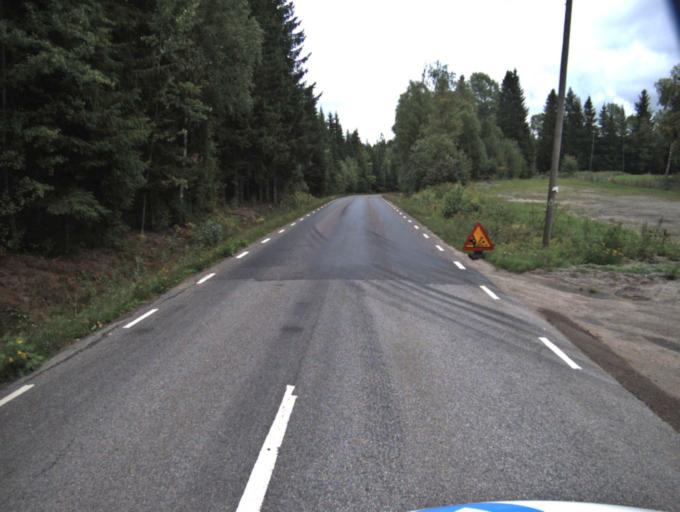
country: SE
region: Vaestra Goetaland
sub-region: Ulricehamns Kommun
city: Ulricehamn
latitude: 57.7699
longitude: 13.4505
